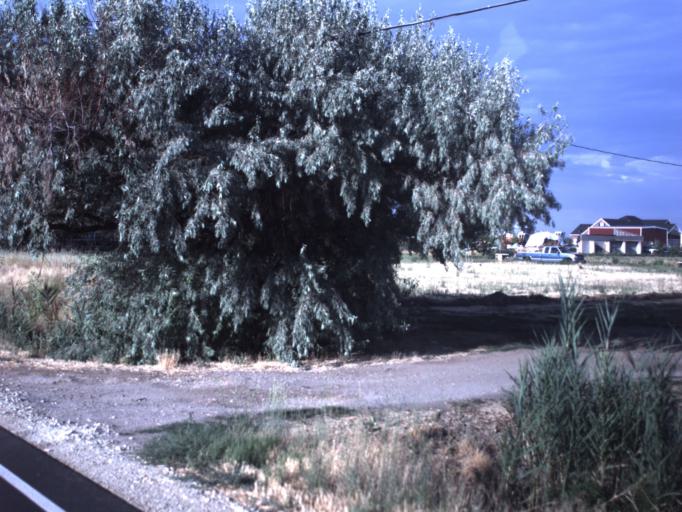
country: US
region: Utah
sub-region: Weber County
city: Plain City
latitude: 41.2548
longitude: -112.0925
